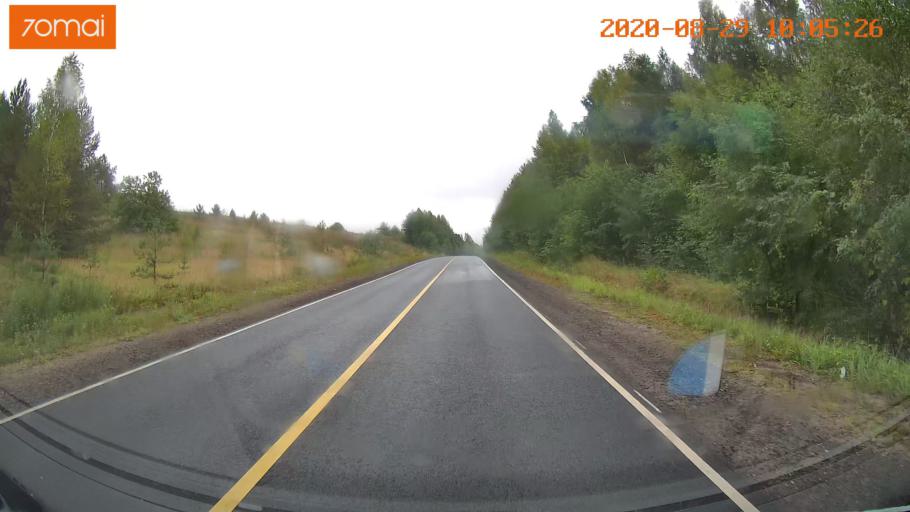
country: RU
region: Ivanovo
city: Zarechnyy
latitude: 57.3928
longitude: 42.5214
